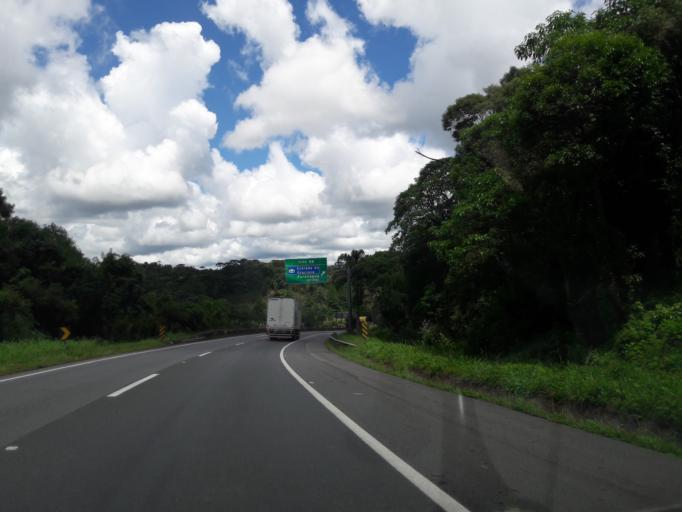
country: BR
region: Parana
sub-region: Campina Grande Do Sul
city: Campina Grande do Sul
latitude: -25.3024
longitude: -48.9431
